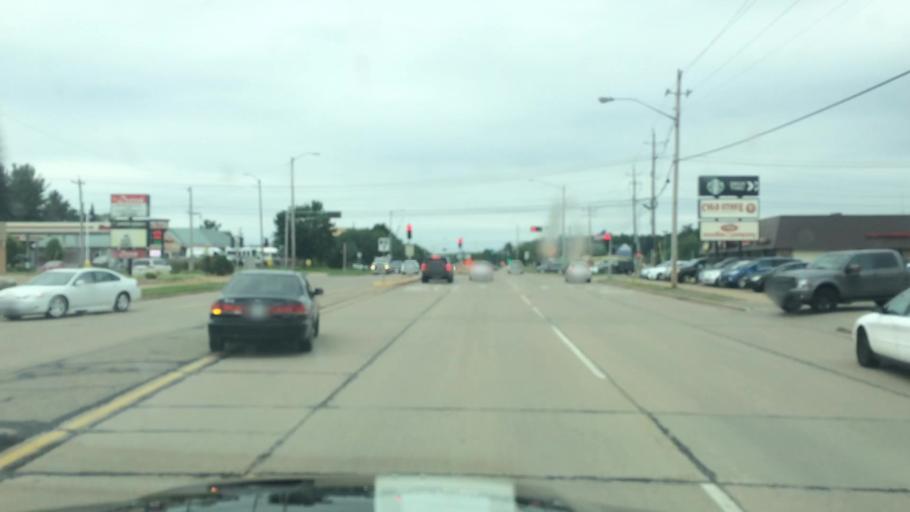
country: US
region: Wisconsin
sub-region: Portage County
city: Stevens Point
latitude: 44.5332
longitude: -89.5749
